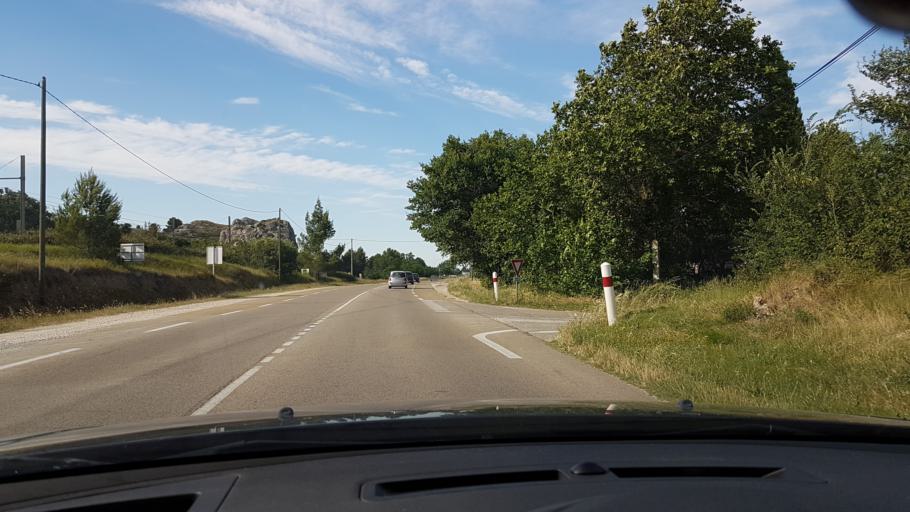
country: FR
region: Provence-Alpes-Cote d'Azur
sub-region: Departement des Bouches-du-Rhone
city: Graveson
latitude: 43.8720
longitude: 4.7719
